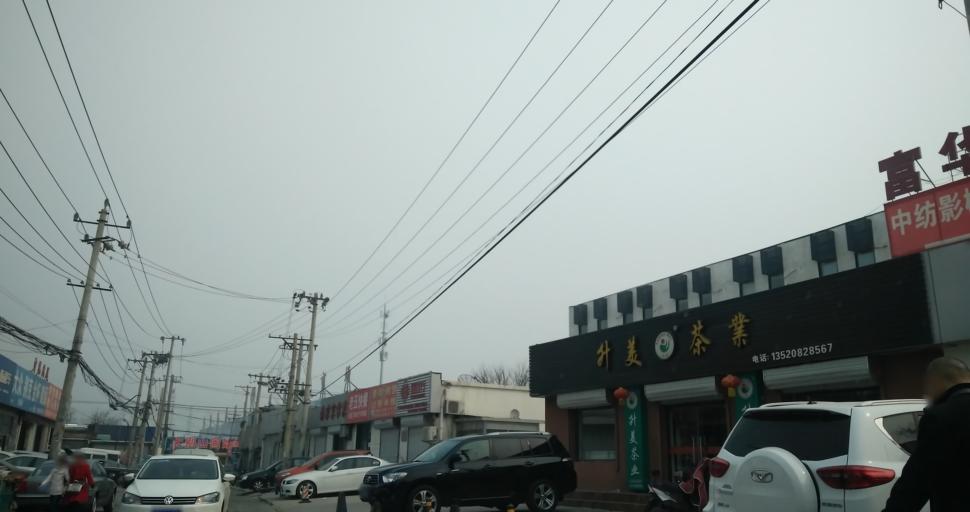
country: CN
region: Beijing
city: Jiugong
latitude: 39.8490
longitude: 116.4804
